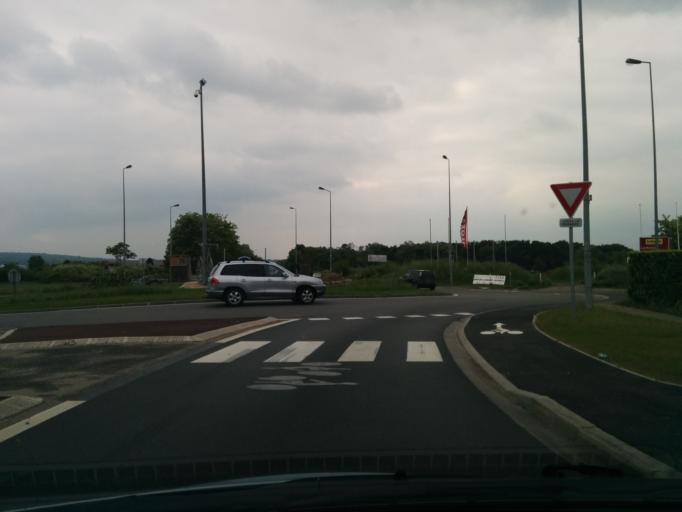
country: FR
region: Ile-de-France
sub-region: Departement des Yvelines
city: Mezy-sur-Seine
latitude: 48.9841
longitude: 1.8924
